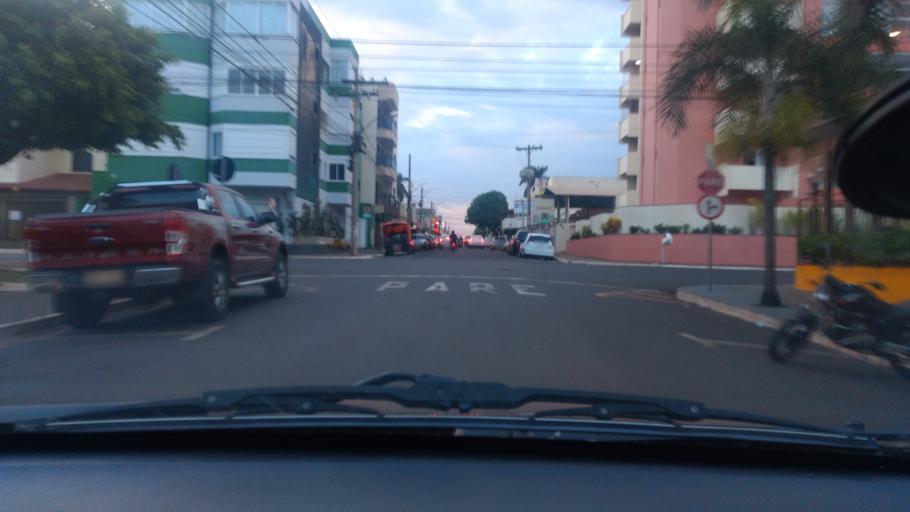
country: BR
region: Goias
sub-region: Santa Helena De Goias
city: Santa Helena de Goias
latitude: -17.7957
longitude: -50.9303
